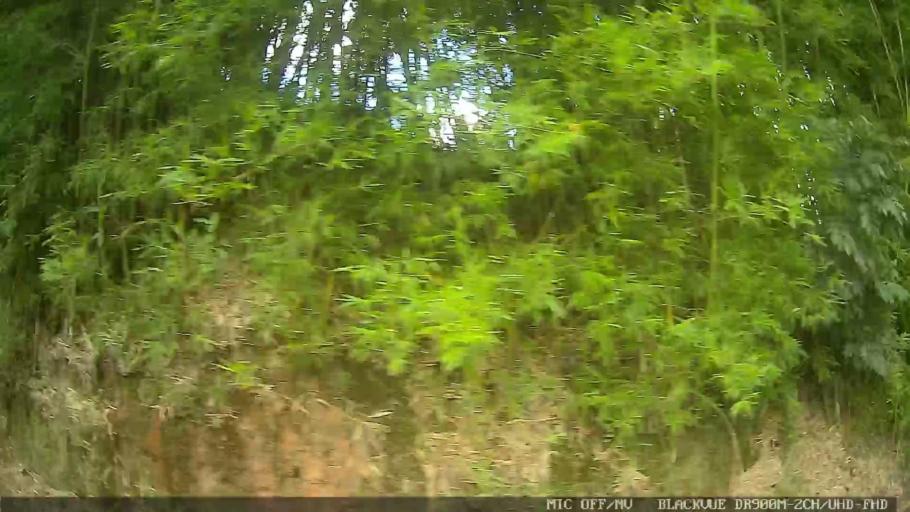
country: BR
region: Sao Paulo
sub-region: Braganca Paulista
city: Braganca Paulista
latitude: -23.0028
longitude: -46.4881
